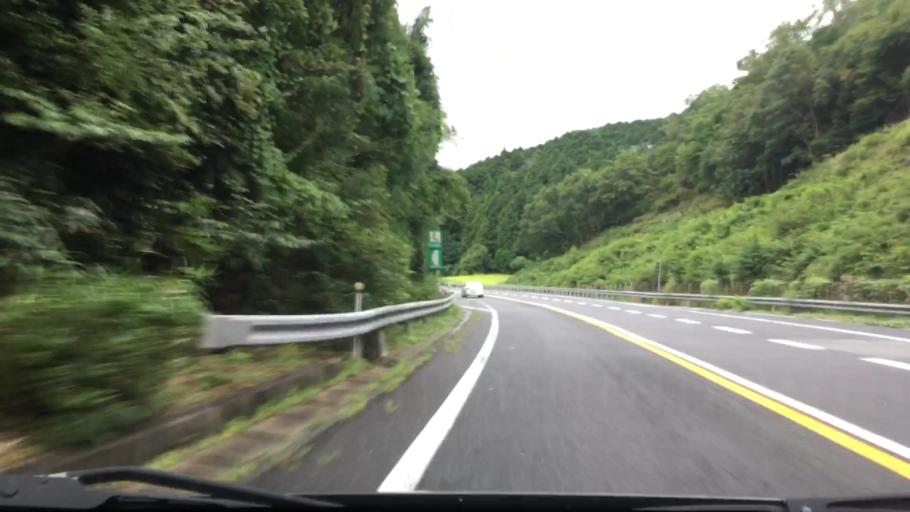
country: JP
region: Hyogo
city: Nishiwaki
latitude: 35.0952
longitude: 134.7758
